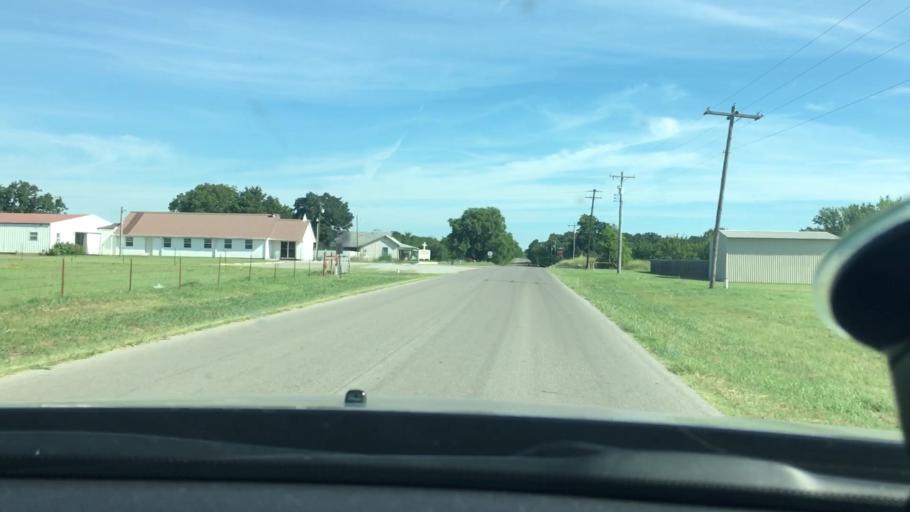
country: US
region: Oklahoma
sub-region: Carter County
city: Lone Grove
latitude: 34.2443
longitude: -97.2474
